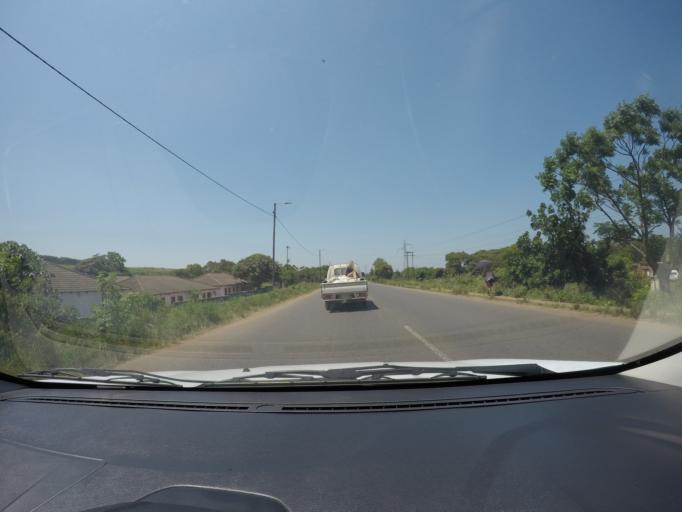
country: ZA
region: KwaZulu-Natal
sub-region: uThungulu District Municipality
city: eSikhawini
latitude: -28.8368
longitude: 31.9372
